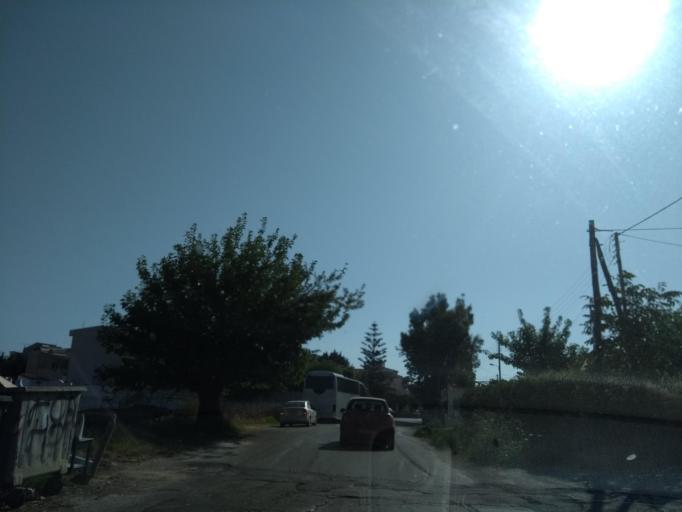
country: GR
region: Crete
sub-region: Nomos Chanias
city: Georgioupolis
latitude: 35.3474
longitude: 24.2966
